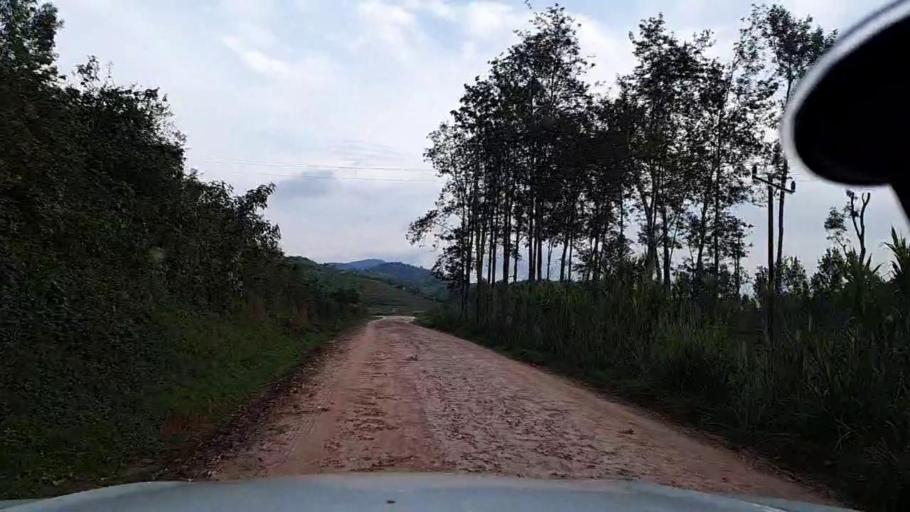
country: RW
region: Southern Province
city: Nyanza
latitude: -2.2125
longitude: 29.6186
